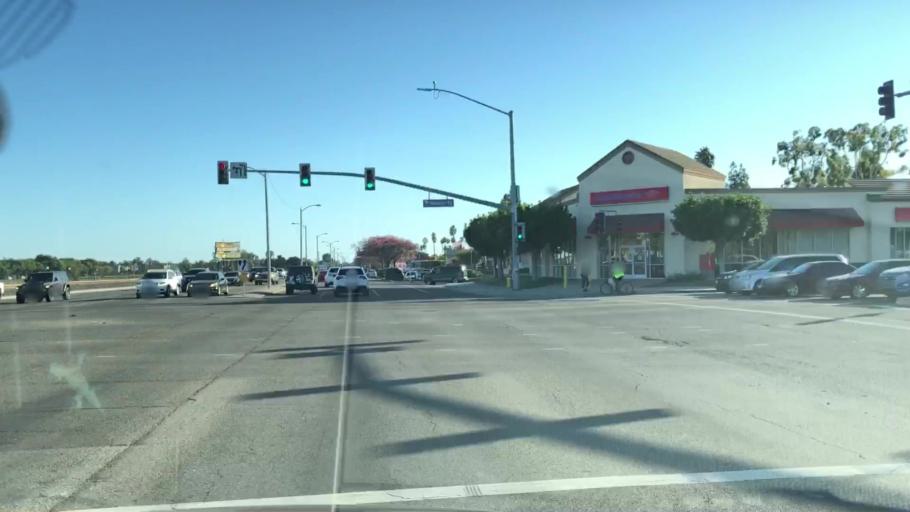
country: US
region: California
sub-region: Ventura County
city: El Rio
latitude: 34.2193
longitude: -119.1772
